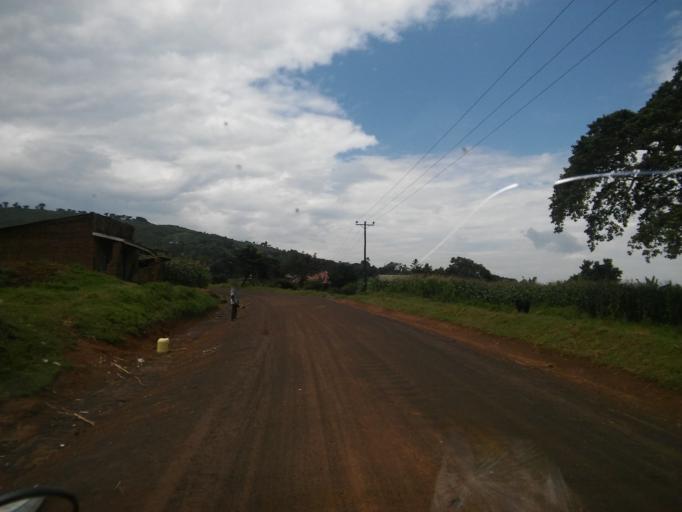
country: UG
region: Eastern Region
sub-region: Tororo District
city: Tororo
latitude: 0.8146
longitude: 34.3053
